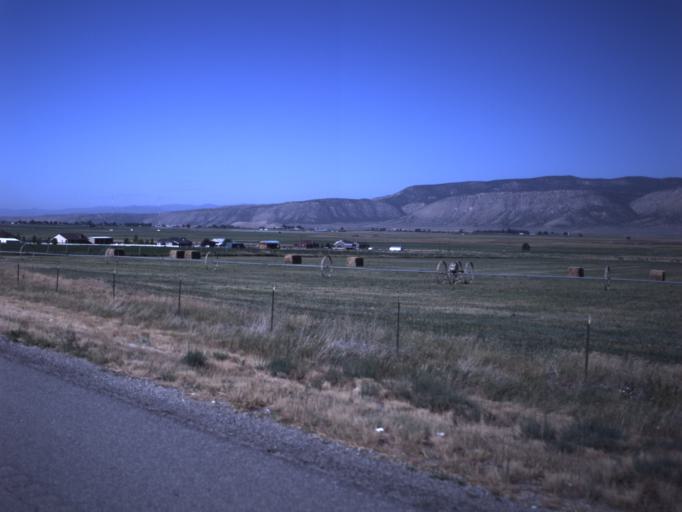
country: US
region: Utah
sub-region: Sanpete County
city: Manti
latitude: 39.3103
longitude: -111.6124
